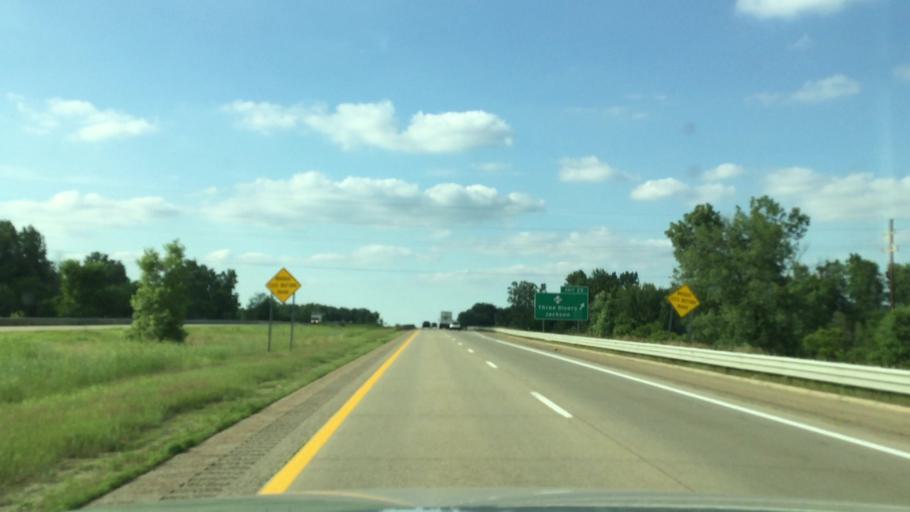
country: US
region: Michigan
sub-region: Branch County
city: Union City
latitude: 42.0978
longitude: -84.9967
